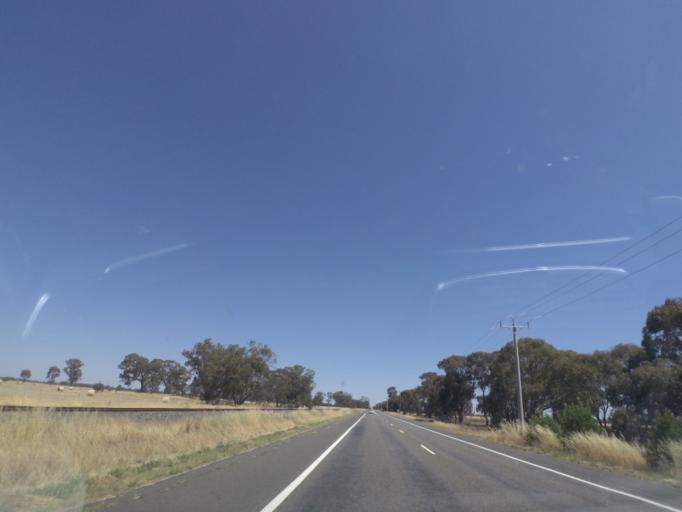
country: AU
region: Victoria
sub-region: Greater Shepparton
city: Shepparton
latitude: -36.1970
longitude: 145.4318
